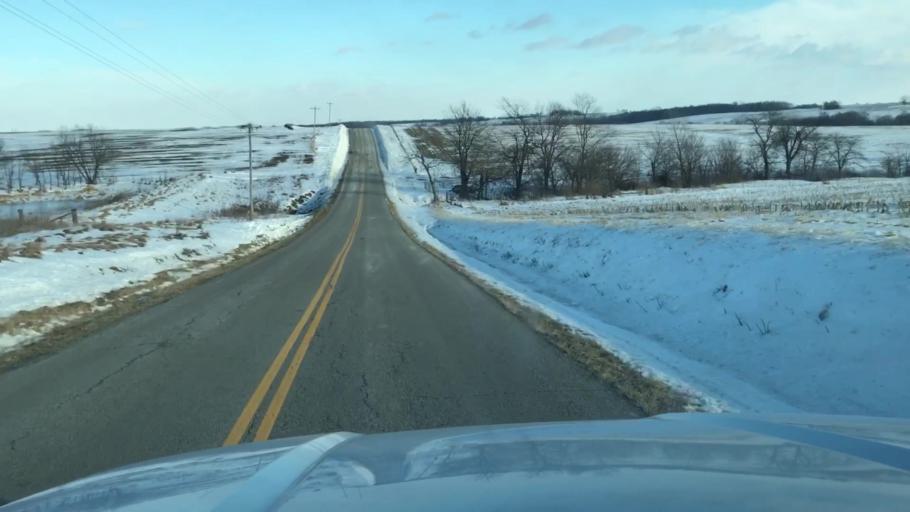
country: US
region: Missouri
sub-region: Holt County
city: Oregon
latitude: 40.1006
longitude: -94.9883
